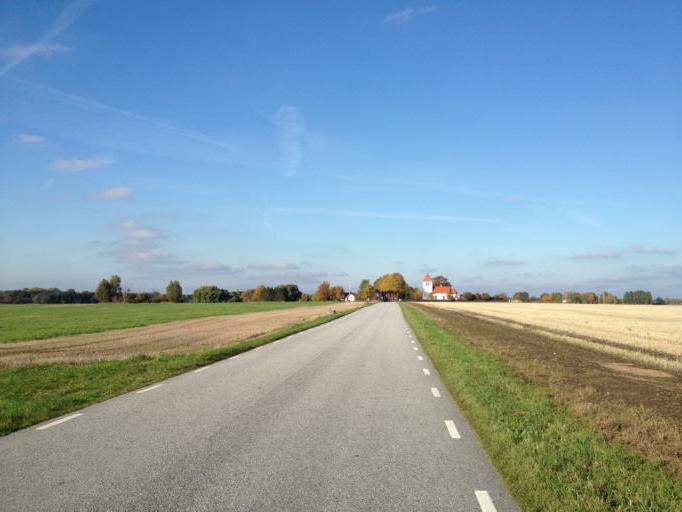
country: SE
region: Skane
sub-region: Kavlinge Kommun
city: Hofterup
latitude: 55.7807
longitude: 12.9754
